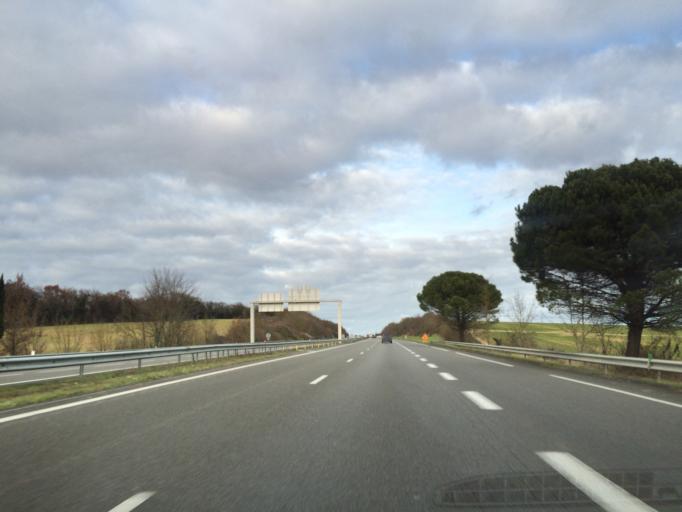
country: FR
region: Poitou-Charentes
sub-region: Departement de la Charente-Maritime
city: Saint-Jean-d'Angely
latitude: 45.9695
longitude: -0.5489
